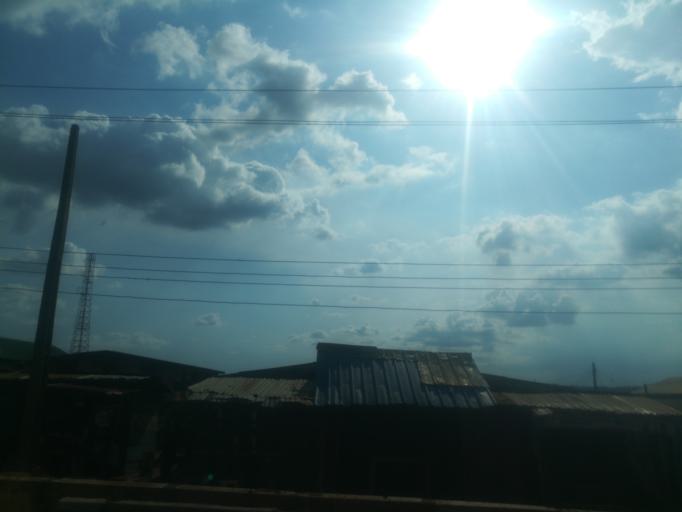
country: NG
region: Oyo
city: Ibadan
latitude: 7.4237
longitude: 3.8430
